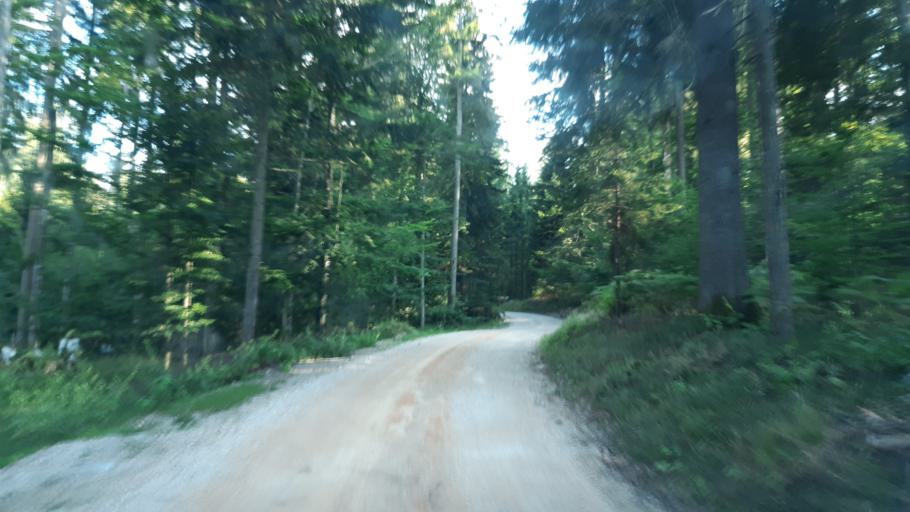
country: SI
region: Dolenjske Toplice
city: Dolenjske Toplice
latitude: 45.6959
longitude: 15.0126
